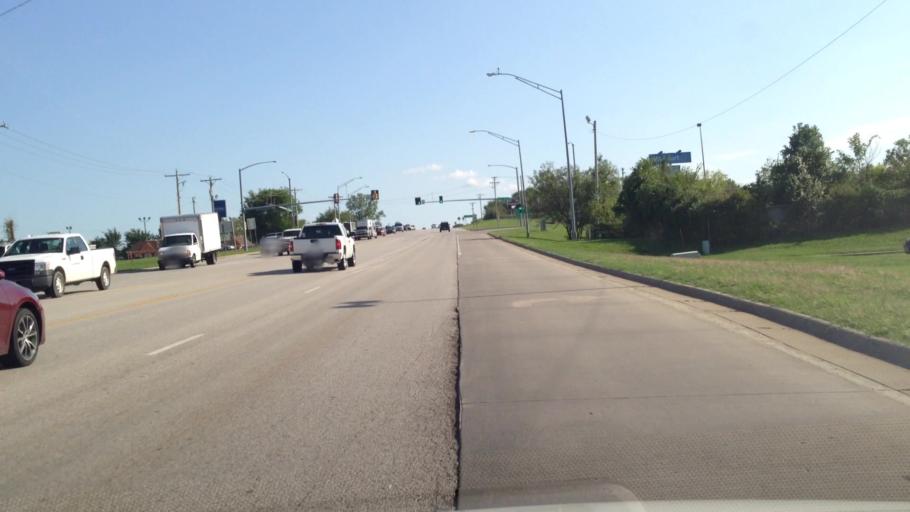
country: US
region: Kansas
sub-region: Bourbon County
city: Fort Scott
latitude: 37.8098
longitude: -94.7055
